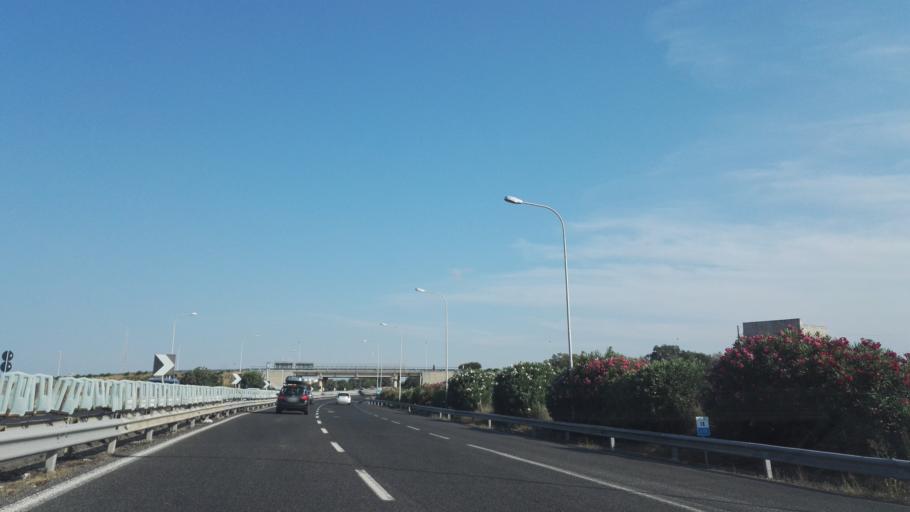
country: IT
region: Apulia
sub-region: Provincia di Bari
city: Mola di Bari
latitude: 41.0706
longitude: 17.0641
